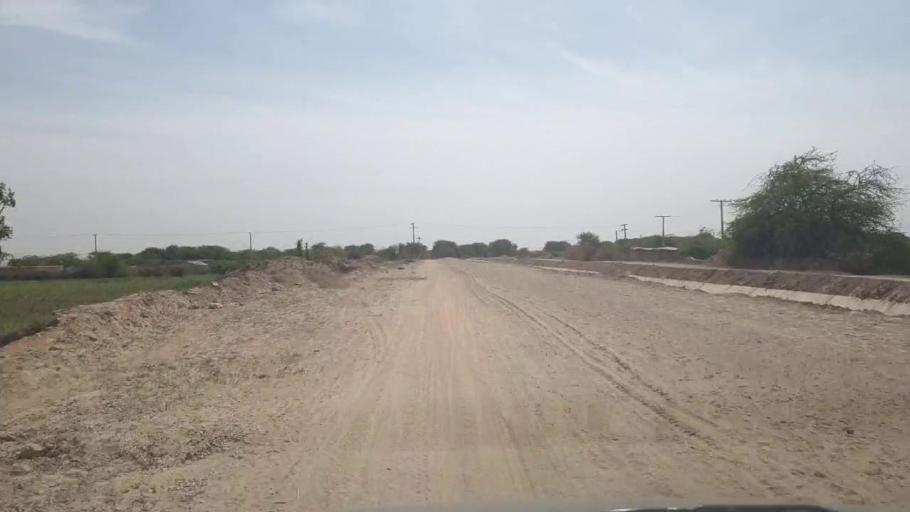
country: PK
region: Sindh
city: Kunri
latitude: 25.2276
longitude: 69.6575
